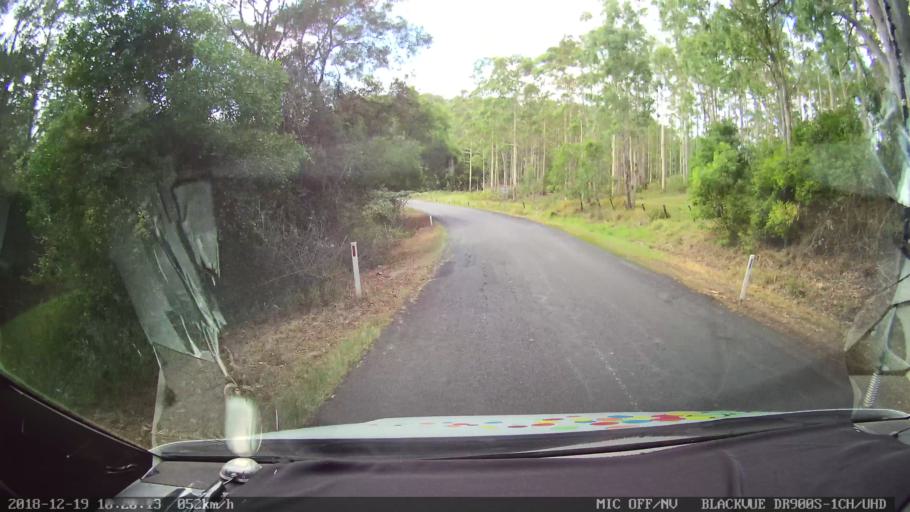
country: AU
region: New South Wales
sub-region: Kyogle
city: Kyogle
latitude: -28.6020
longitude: 153.0515
